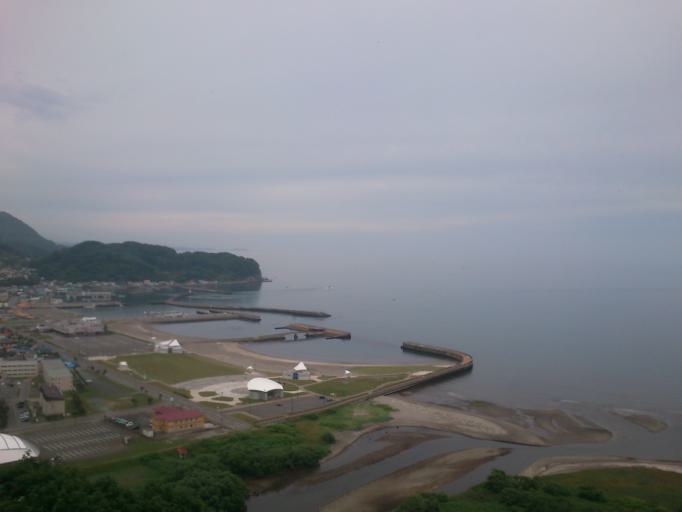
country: JP
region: Hokkaido
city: Niseko Town
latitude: 42.5889
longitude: 140.6988
